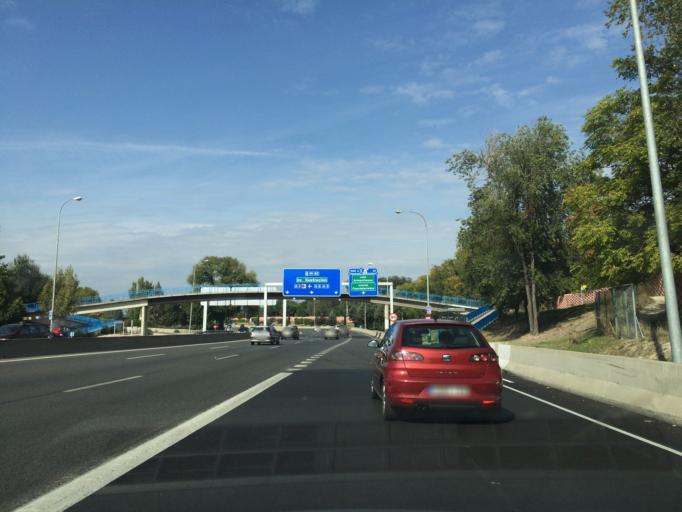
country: ES
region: Madrid
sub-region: Provincia de Madrid
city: Moncloa-Aravaca
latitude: 40.4586
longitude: -3.7449
